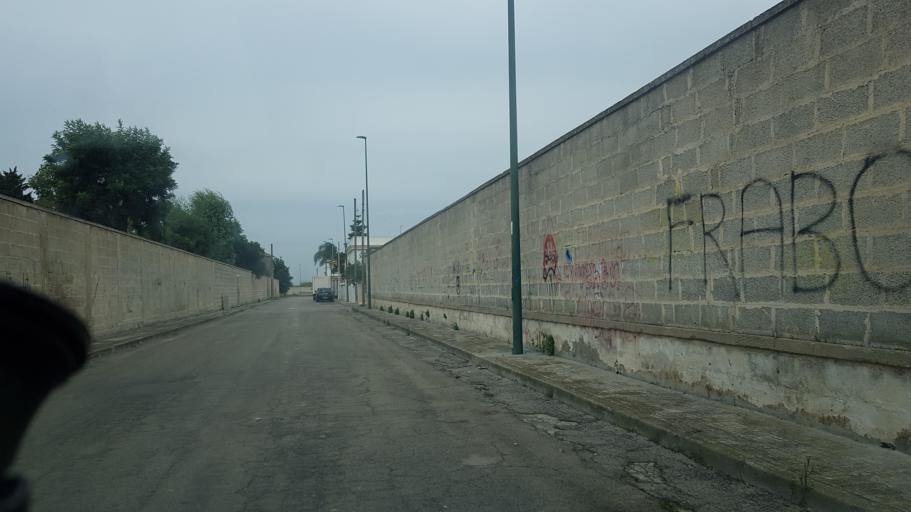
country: IT
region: Apulia
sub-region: Provincia di Lecce
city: Guagnano
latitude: 40.4023
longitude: 17.9413
